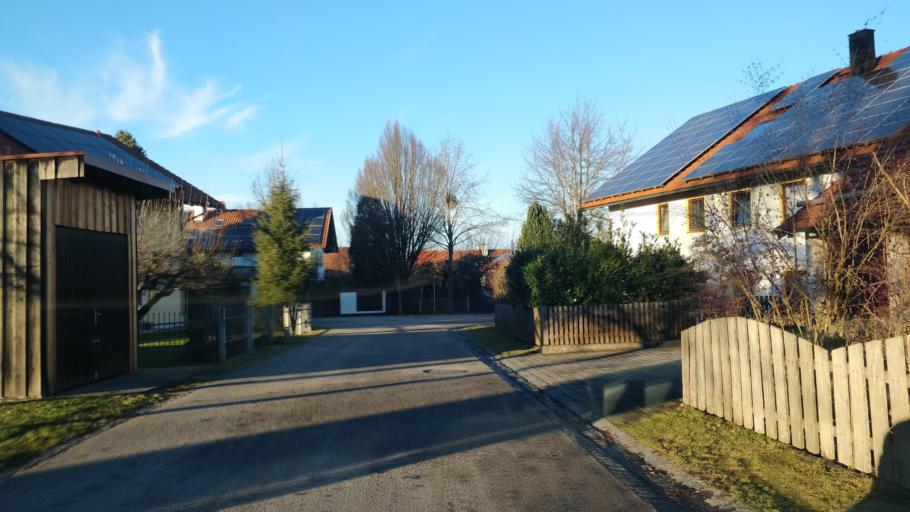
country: DE
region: Bavaria
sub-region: Upper Bavaria
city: Obertaufkirchen
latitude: 48.2591
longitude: 12.2796
